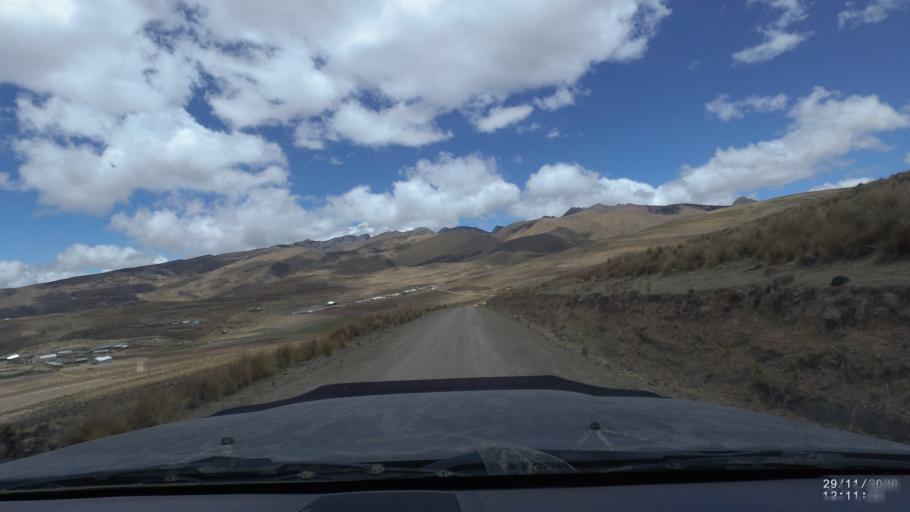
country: BO
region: Cochabamba
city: Cochabamba
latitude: -17.1184
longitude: -66.3050
